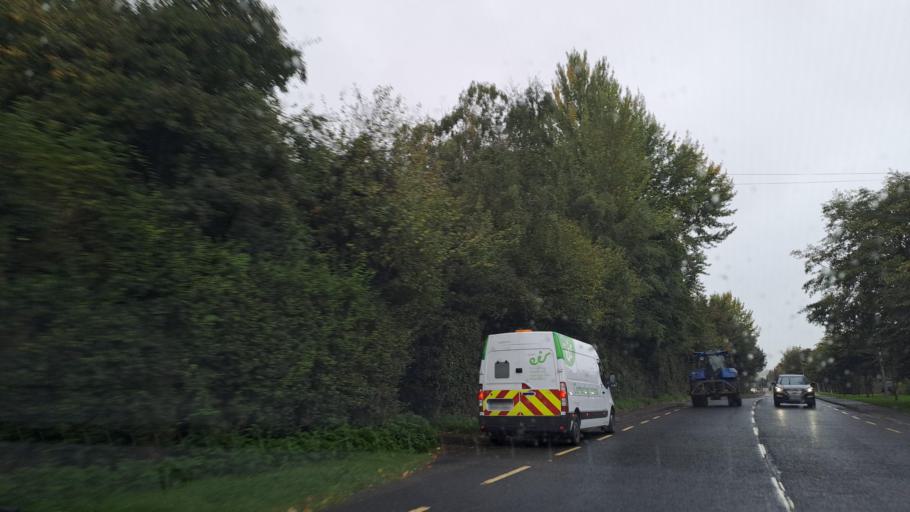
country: IE
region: Ulster
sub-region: County Monaghan
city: Carrickmacross
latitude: 53.9710
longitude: -6.7050
